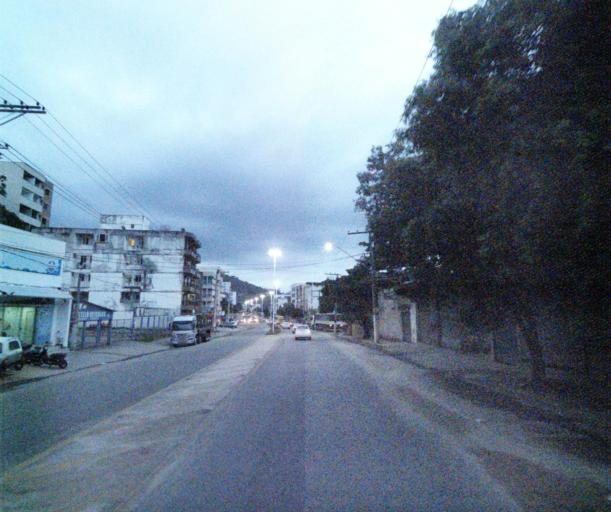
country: BR
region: Espirito Santo
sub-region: Castelo
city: Castelo
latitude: -20.6165
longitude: -41.2043
